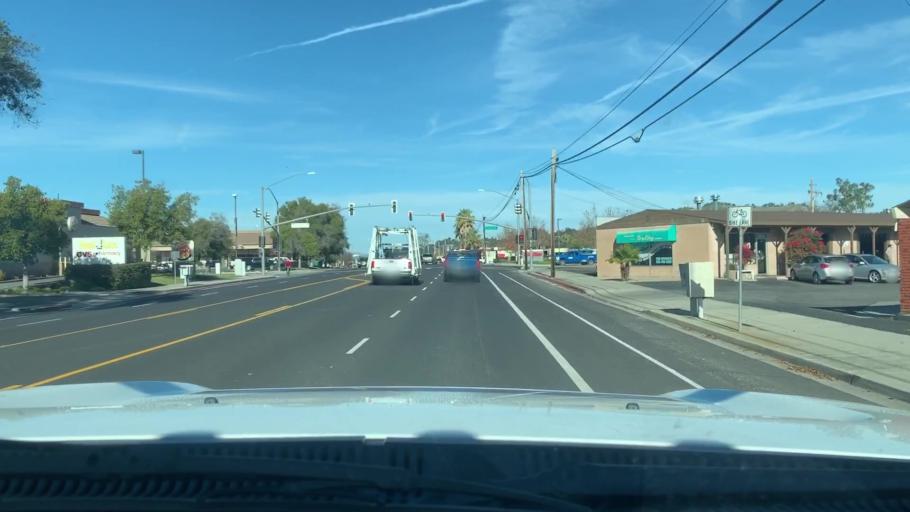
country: US
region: California
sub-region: San Luis Obispo County
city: Atascadero
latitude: 35.4742
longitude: -120.6543
